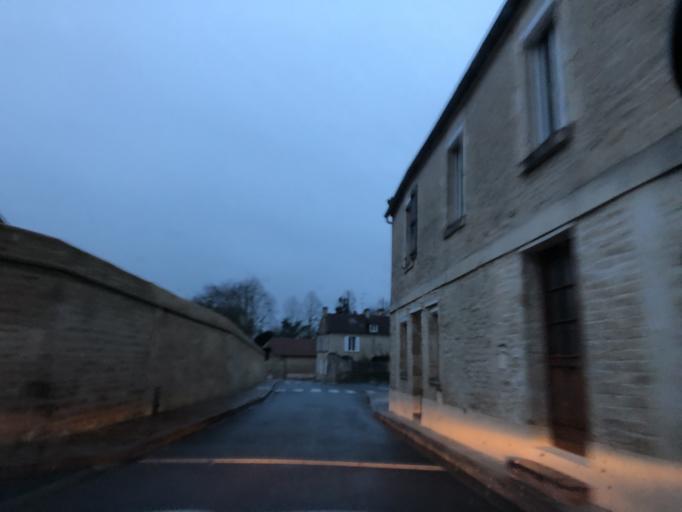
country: FR
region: Lower Normandy
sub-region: Departement du Calvados
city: Mathieu
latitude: 49.2541
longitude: -0.3688
